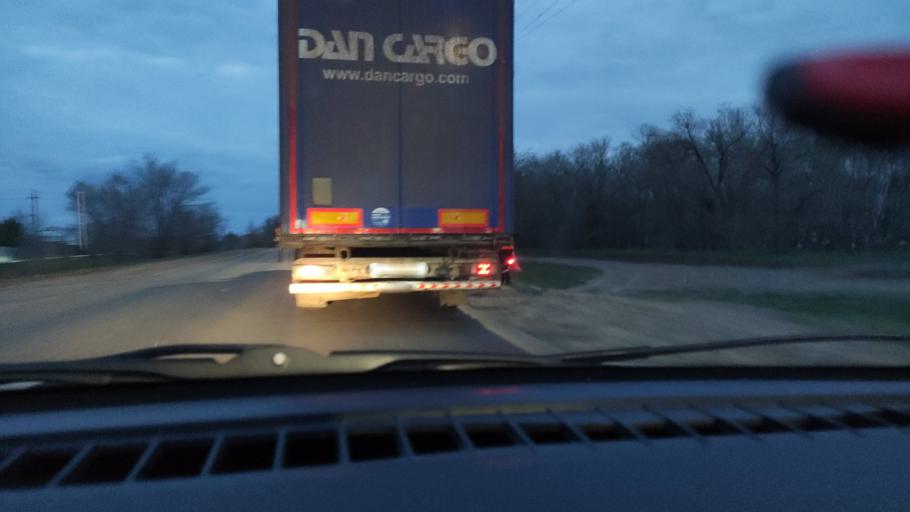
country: RU
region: Orenburg
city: Tatarskaya Kargala
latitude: 51.8736
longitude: 55.1458
